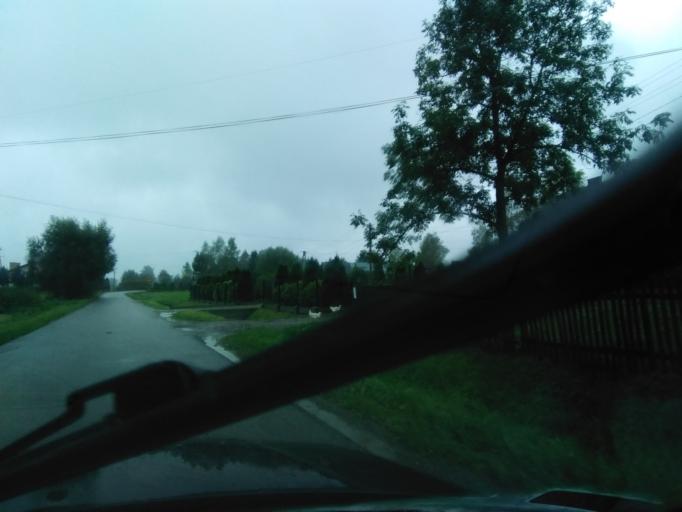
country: PL
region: Subcarpathian Voivodeship
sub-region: Powiat ropczycko-sedziszowski
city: Niedzwiada
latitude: 50.0065
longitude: 21.5504
